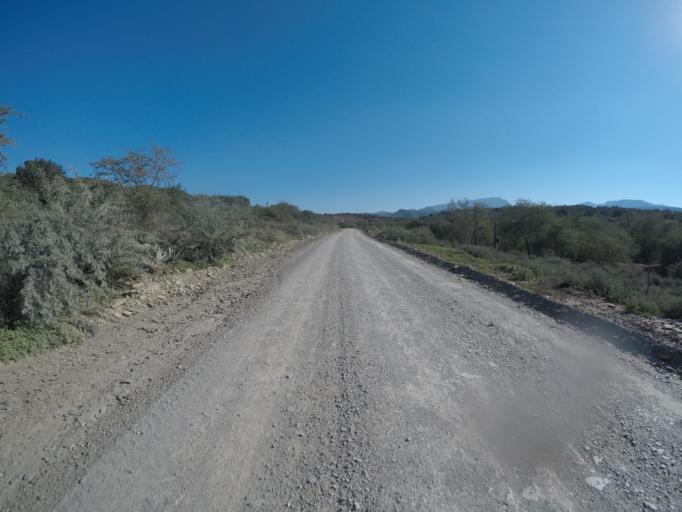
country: ZA
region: Eastern Cape
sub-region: Cacadu District Municipality
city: Kruisfontein
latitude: -33.6755
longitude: 24.5785
